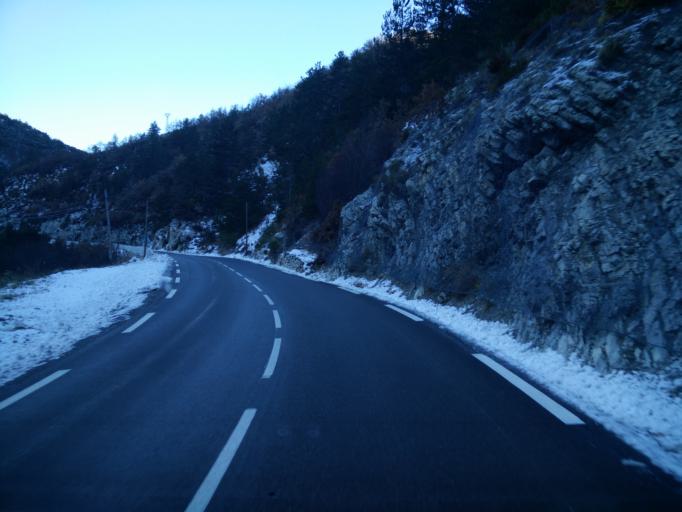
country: FR
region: Provence-Alpes-Cote d'Azur
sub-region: Departement des Alpes-de-Haute-Provence
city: Annot
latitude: 43.9326
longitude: 6.6465
